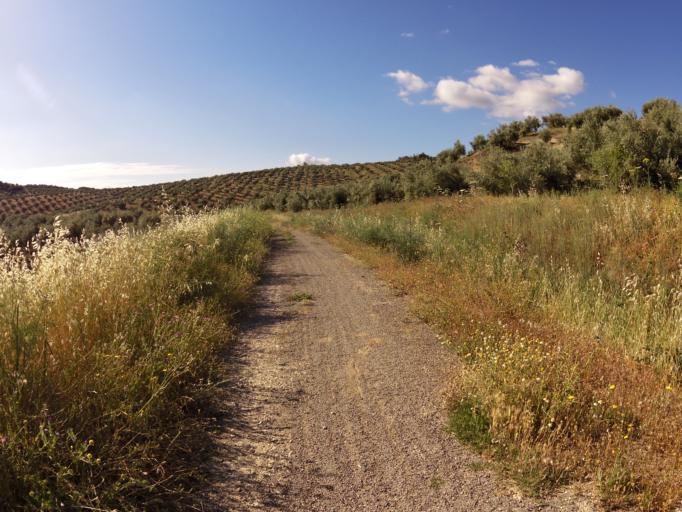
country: ES
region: Andalusia
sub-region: Province of Cordoba
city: Fuente-Tojar
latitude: 37.5800
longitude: -4.1847
